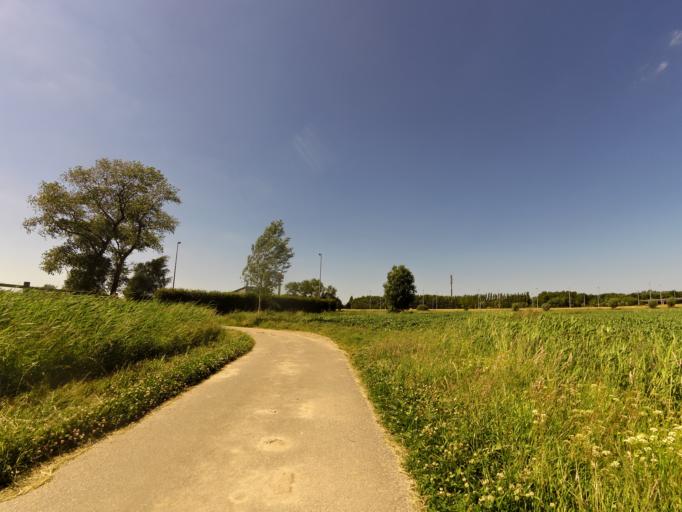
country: BE
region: Flanders
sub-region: Provincie West-Vlaanderen
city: Jabbeke
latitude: 51.1890
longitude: 3.0691
